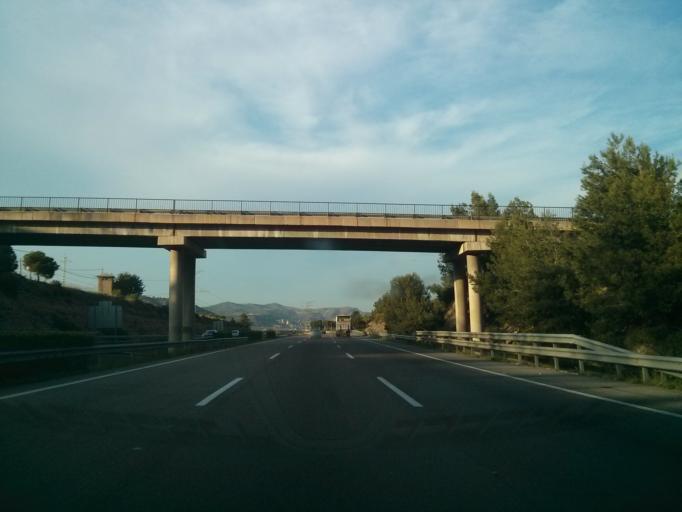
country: ES
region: Valencia
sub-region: Provincia de Valencia
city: Petres
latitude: 39.6644
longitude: -0.3039
